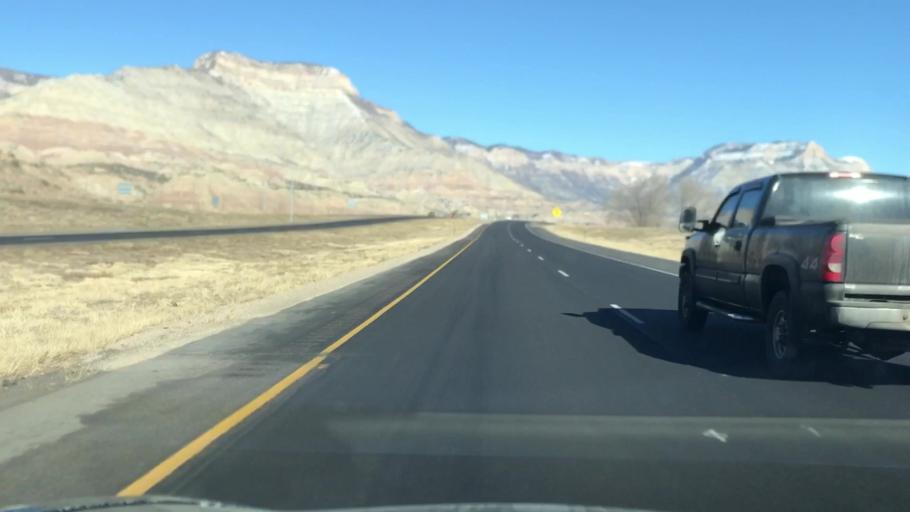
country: US
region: Colorado
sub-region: Garfield County
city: Parachute
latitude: 39.4561
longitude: -108.0476
